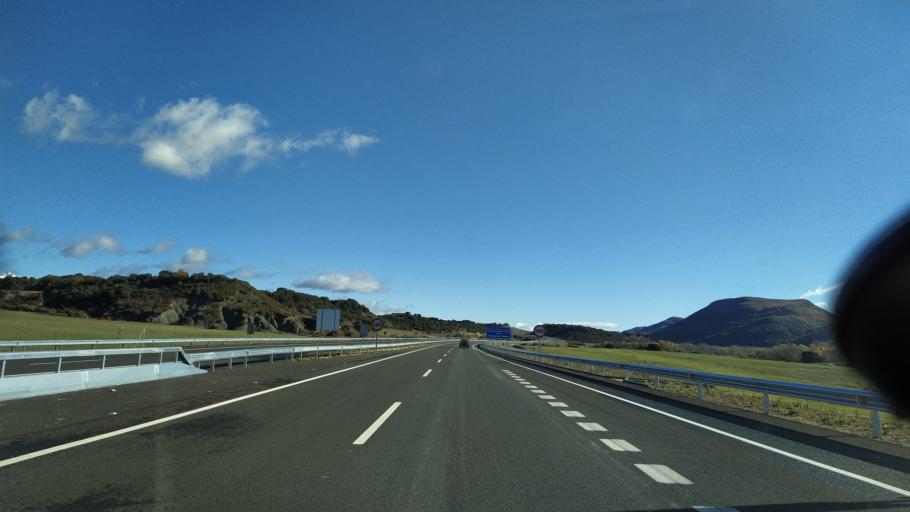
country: ES
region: Aragon
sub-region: Provincia de Huesca
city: Santa Cruz de la Seros
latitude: 42.5646
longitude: -0.7042
